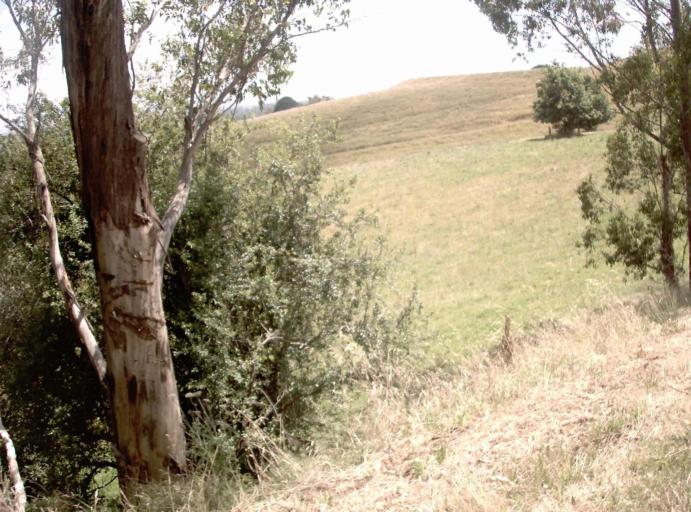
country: AU
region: Victoria
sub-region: Baw Baw
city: Warragul
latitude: -38.2594
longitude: 145.9004
